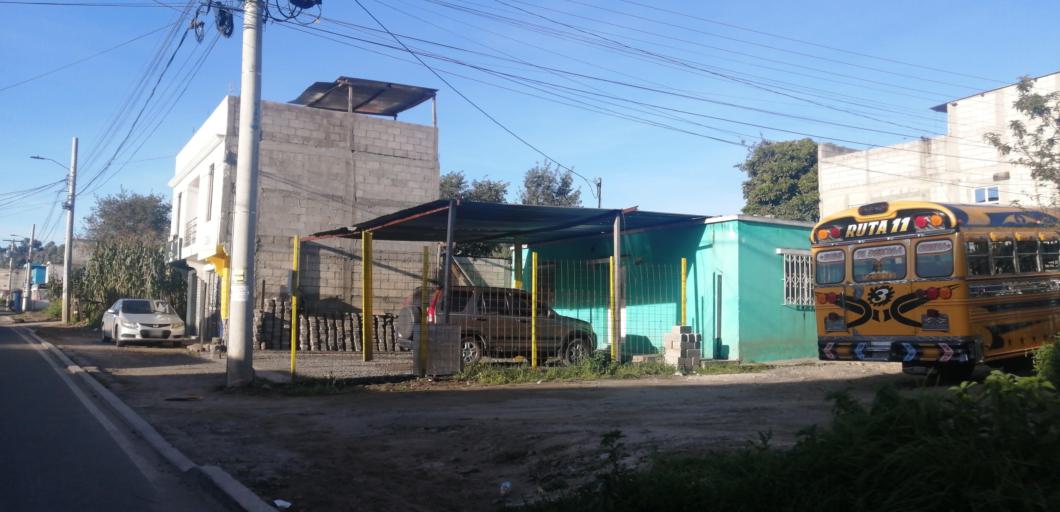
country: GT
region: Quetzaltenango
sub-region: Municipio de La Esperanza
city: La Esperanza
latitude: 14.8637
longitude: -91.5395
